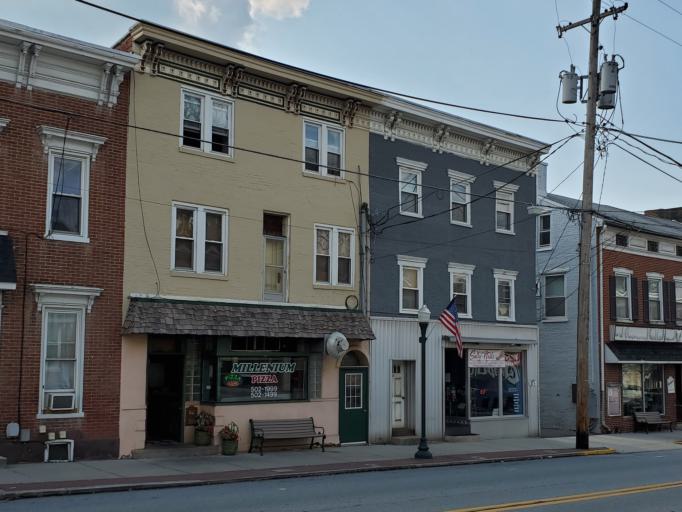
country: US
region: Pennsylvania
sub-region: York County
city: Dillsburg
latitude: 40.1100
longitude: -77.0355
